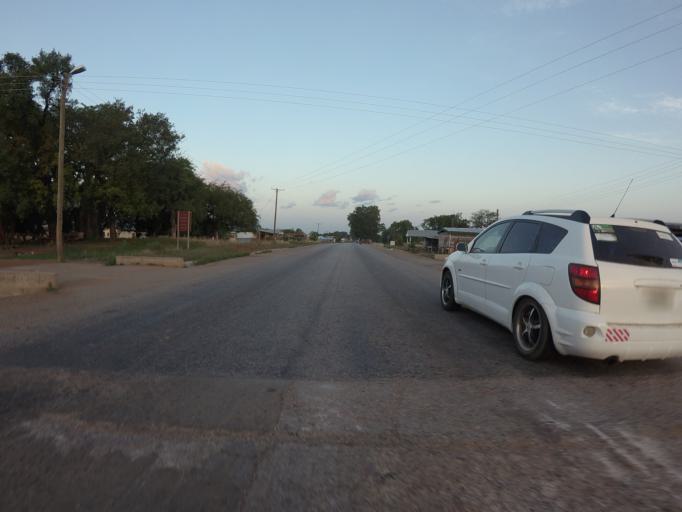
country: GH
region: Upper East
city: Navrongo
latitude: 10.8591
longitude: -1.0295
